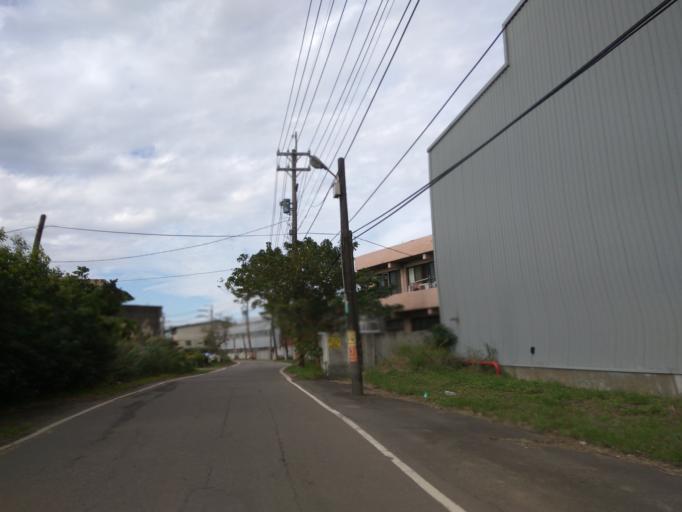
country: TW
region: Taiwan
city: Daxi
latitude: 24.9400
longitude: 121.1746
